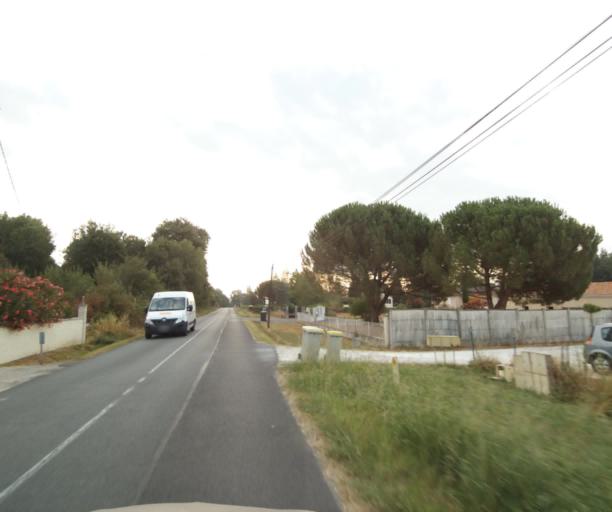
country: FR
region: Aquitaine
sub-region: Departement de la Gironde
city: Creon
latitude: 44.7805
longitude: -0.3339
